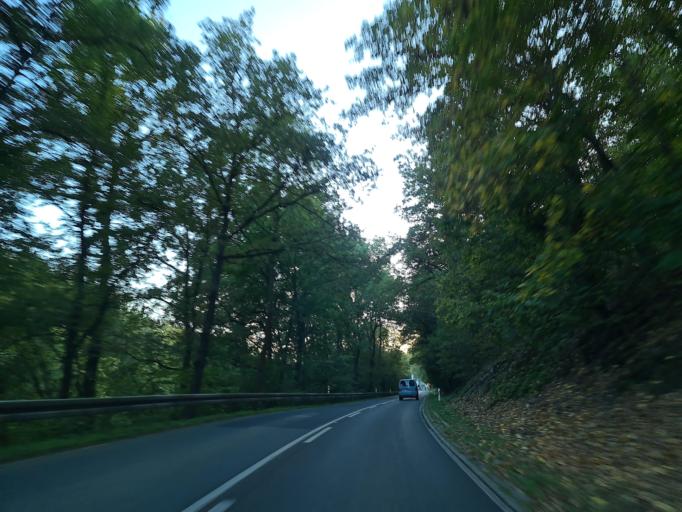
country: DE
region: Saxony
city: Elsterberg
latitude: 50.5927
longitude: 12.1411
